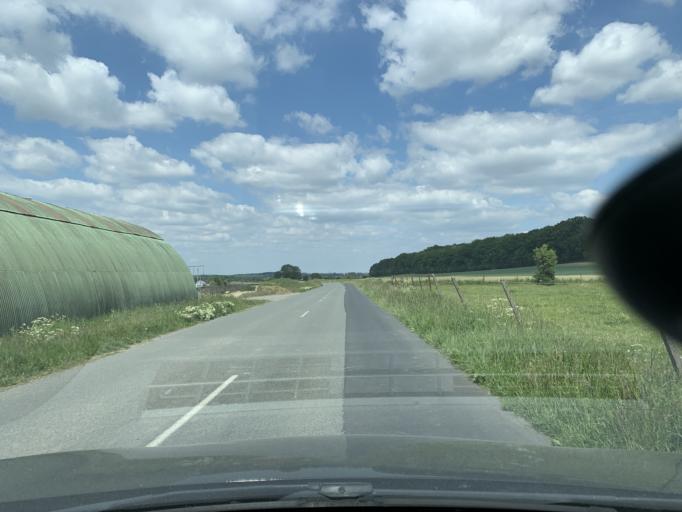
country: FR
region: Nord-Pas-de-Calais
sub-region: Departement du Pas-de-Calais
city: Oisy-le-Verger
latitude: 50.2545
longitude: 3.1137
